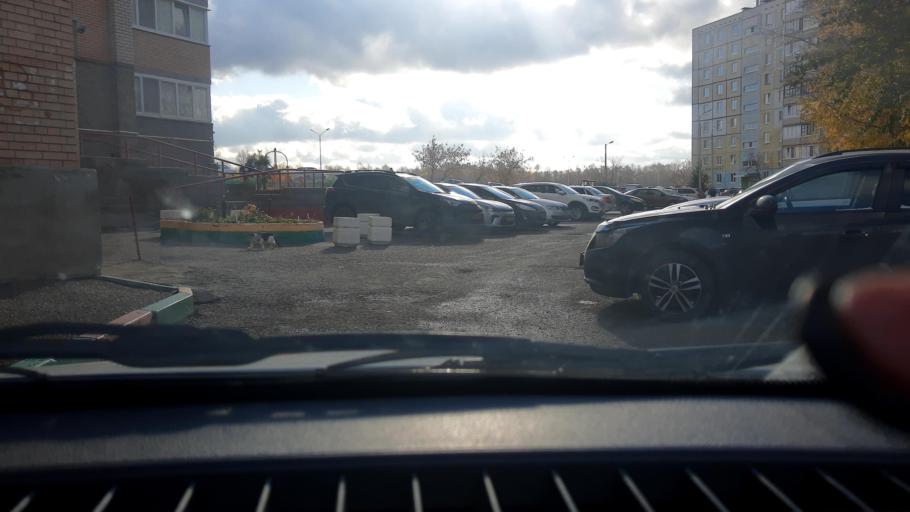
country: RU
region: Bashkortostan
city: Ufa
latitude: 54.7727
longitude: 56.0839
